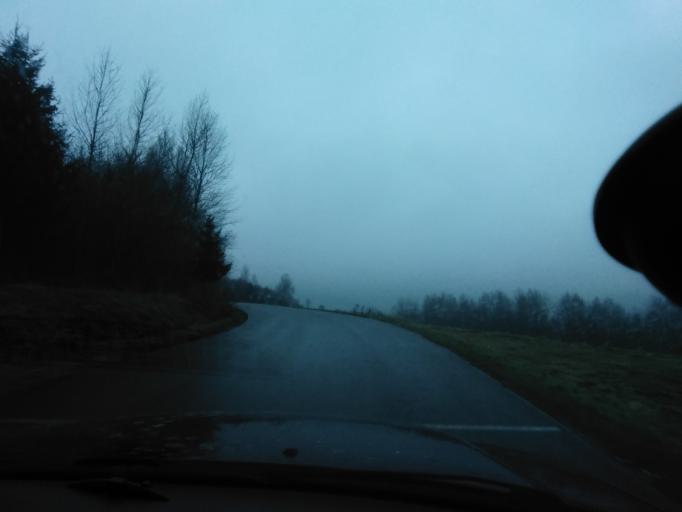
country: PL
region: Subcarpathian Voivodeship
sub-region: Powiat brzozowski
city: Jablonka
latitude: 49.7421
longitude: 22.1109
